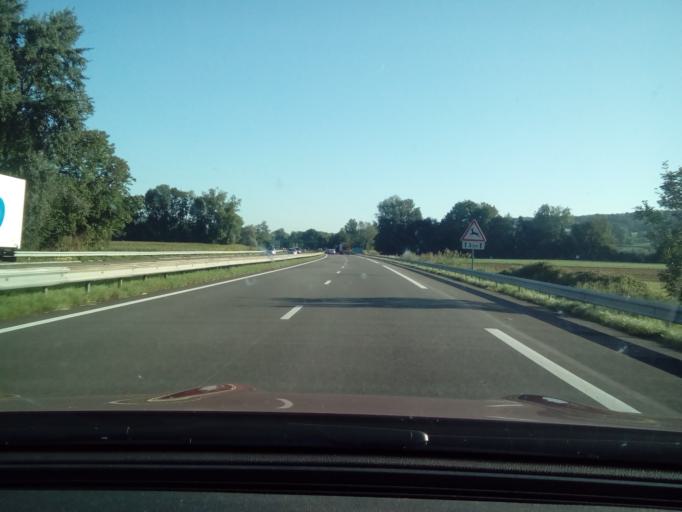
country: FR
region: Rhone-Alpes
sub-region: Departement de la Savoie
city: Albens
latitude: 45.7631
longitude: 5.9555
